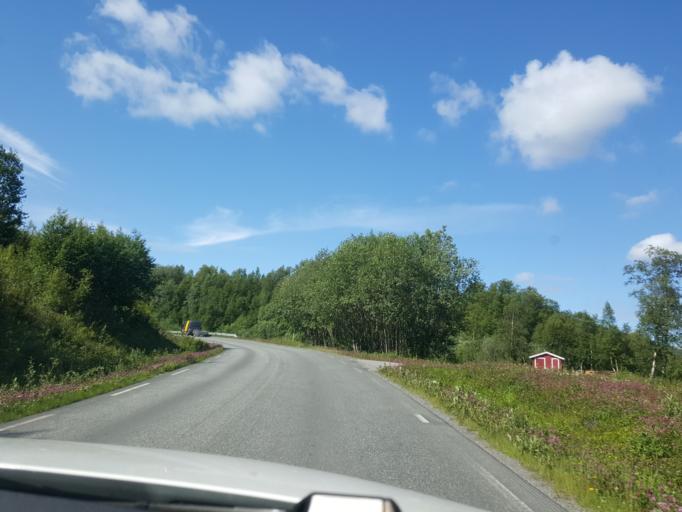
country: NO
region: Nordland
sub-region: Bodo
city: Loding
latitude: 67.1116
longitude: 15.0053
